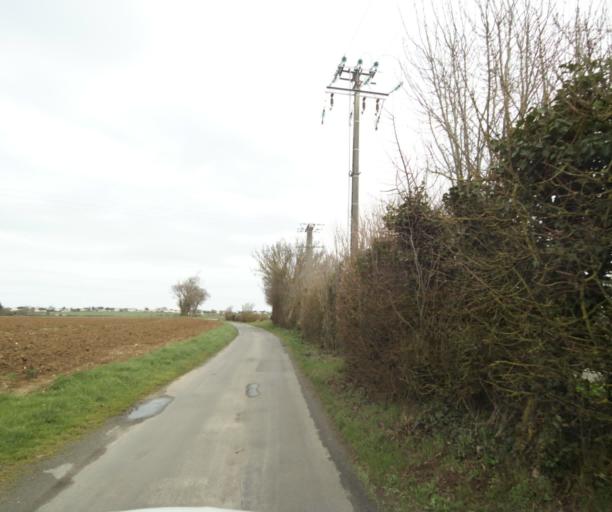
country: FR
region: Poitou-Charentes
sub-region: Departement de la Charente-Maritime
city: Lagord
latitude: 46.1916
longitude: -1.1666
